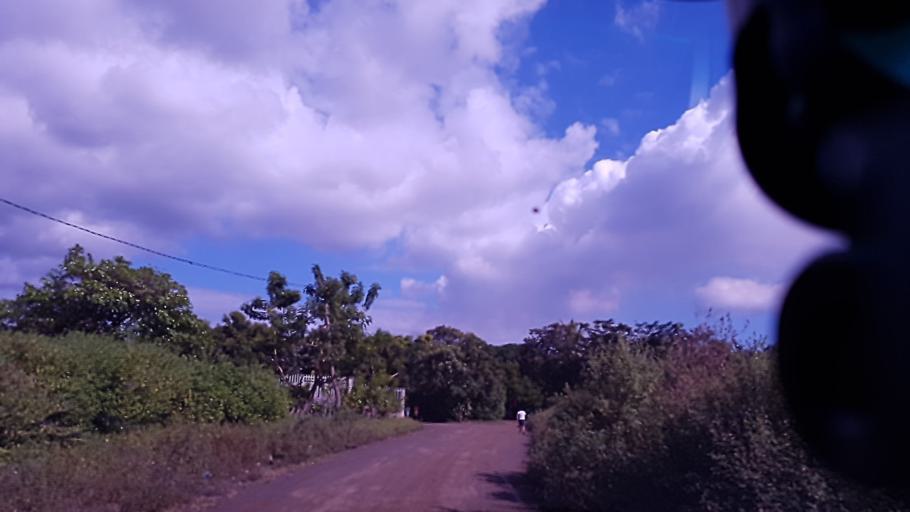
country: NI
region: Masaya
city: Ticuantepe
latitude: 11.9866
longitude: -86.2304
